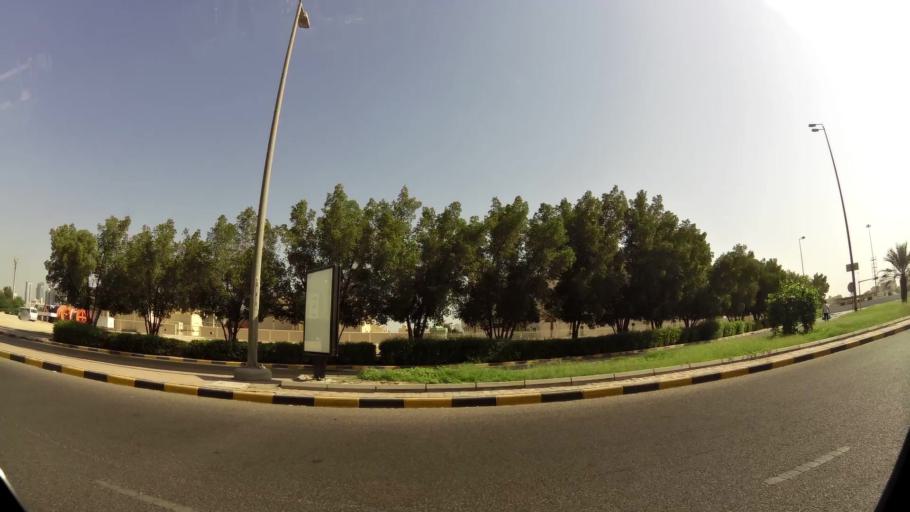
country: KW
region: Al Asimah
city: Kuwait City
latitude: 29.3640
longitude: 47.9845
